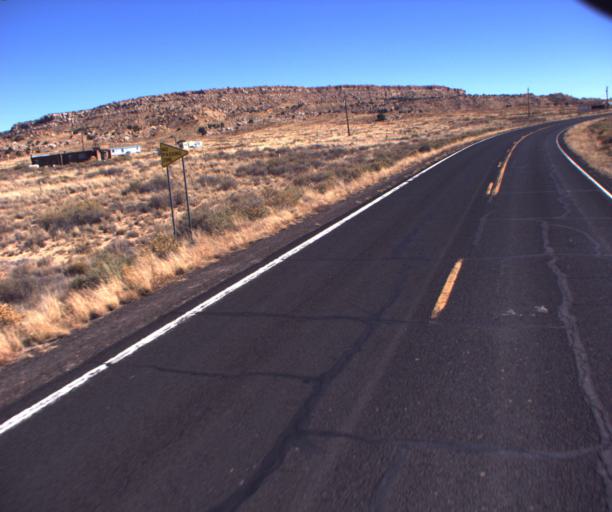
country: US
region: Arizona
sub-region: Navajo County
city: First Mesa
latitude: 35.8389
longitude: -110.3062
